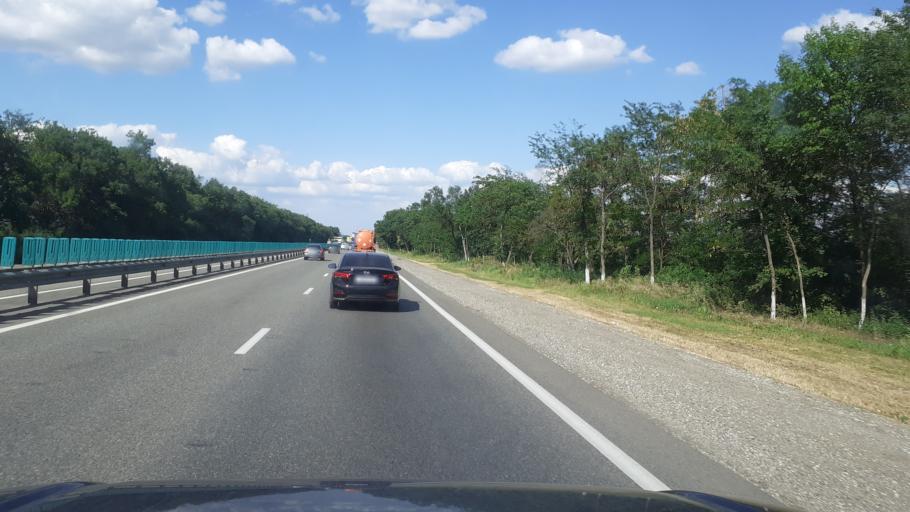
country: RU
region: Krasnodarskiy
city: Severskaya
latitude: 44.8488
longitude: 38.7041
